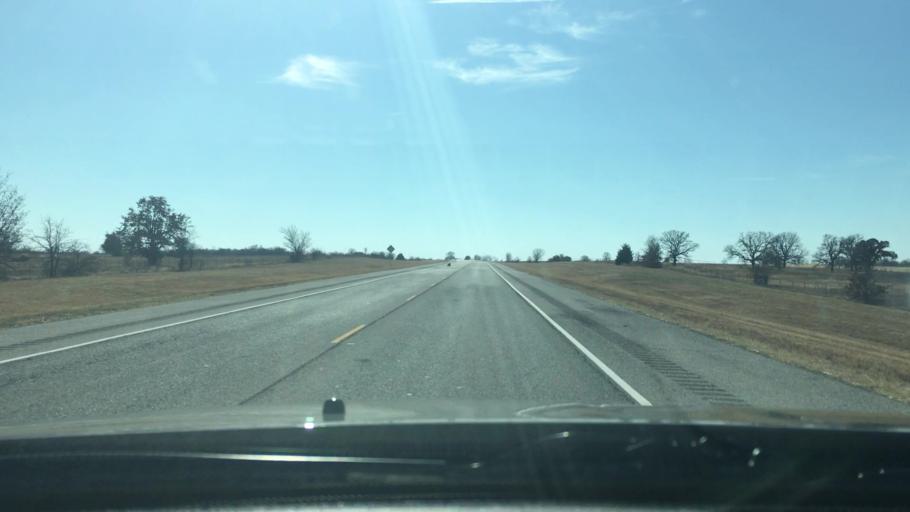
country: US
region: Oklahoma
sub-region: Stephens County
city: Meridian
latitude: 34.4040
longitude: -97.9742
